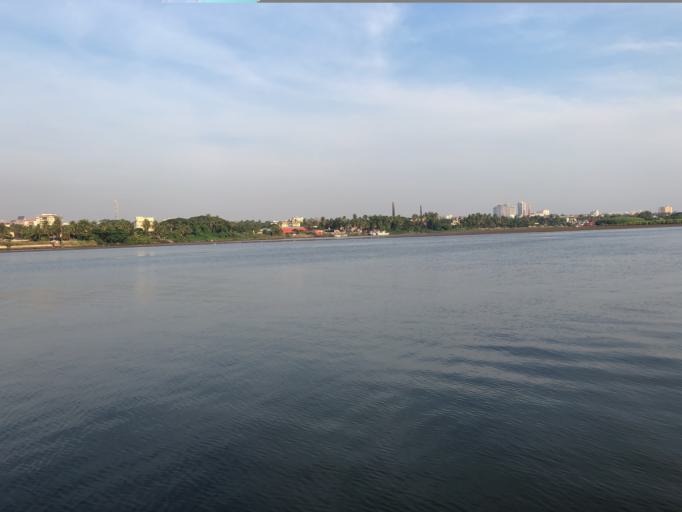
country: IN
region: Karnataka
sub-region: Dakshina Kannada
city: Mangalore
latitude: 12.8825
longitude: 74.8193
